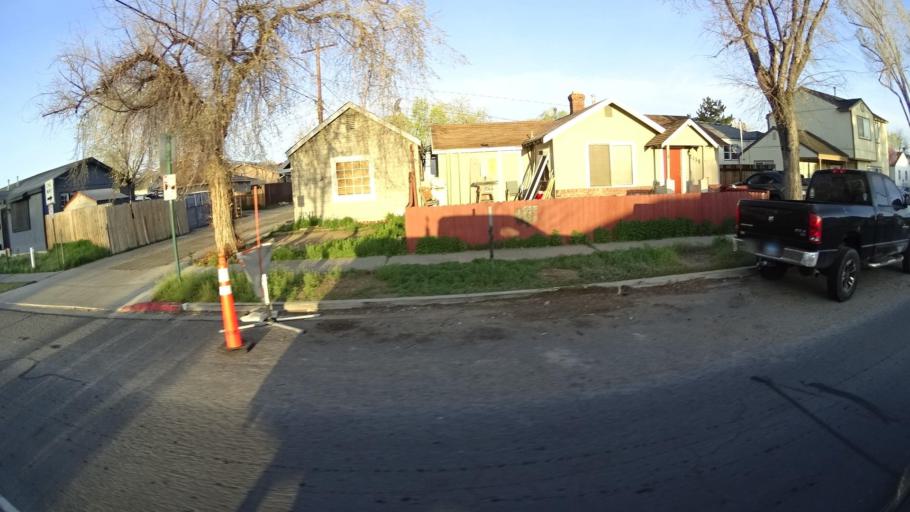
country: US
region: Nevada
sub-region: Washoe County
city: Reno
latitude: 39.5144
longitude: -119.8005
